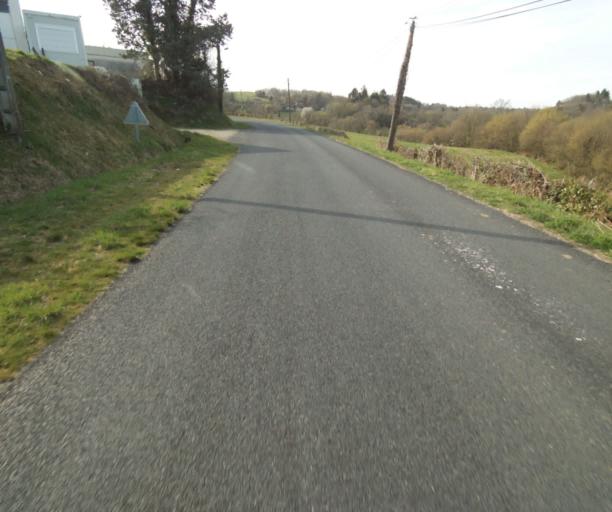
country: FR
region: Limousin
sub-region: Departement de la Correze
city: Tulle
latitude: 45.2880
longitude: 1.7598
